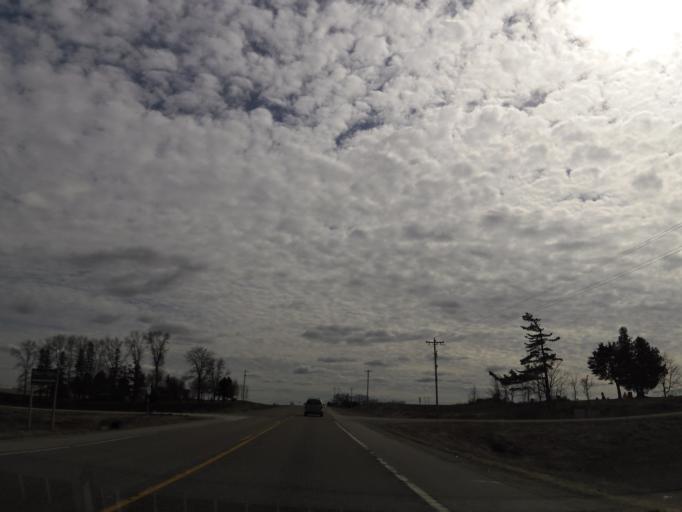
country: US
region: Minnesota
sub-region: Olmsted County
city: Stewartville
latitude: 43.9137
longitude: -92.4085
